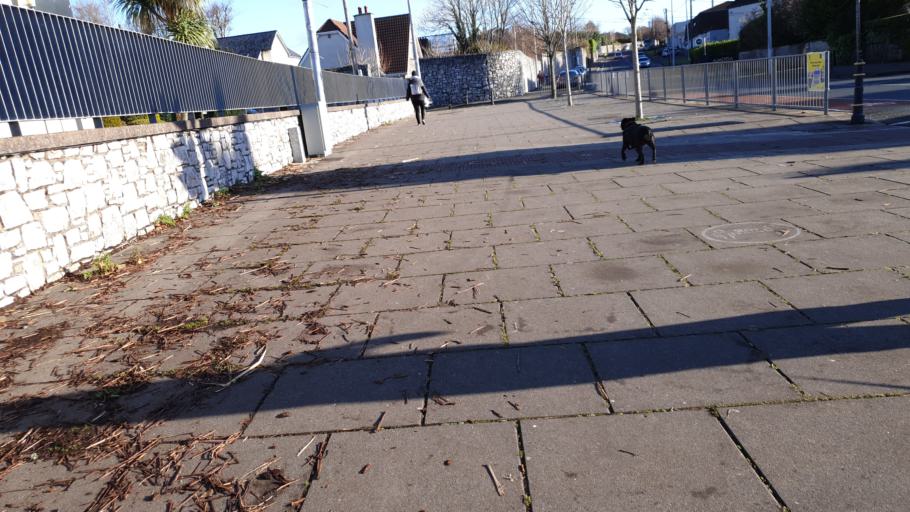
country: IE
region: Munster
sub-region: County Cork
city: Cork
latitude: 51.8921
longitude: -8.4399
